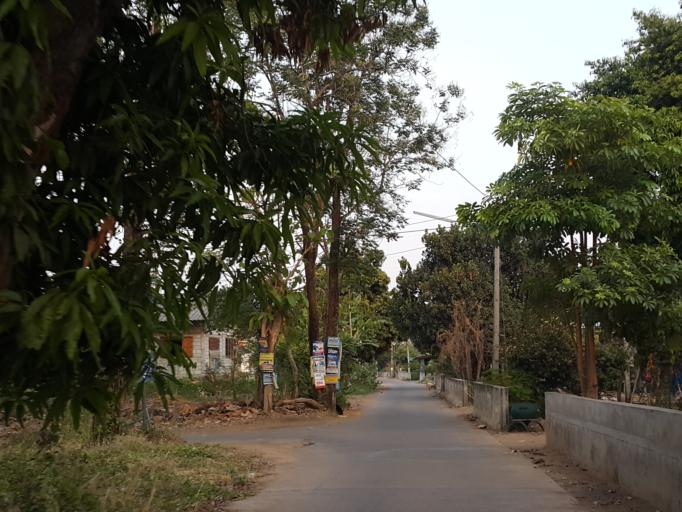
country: TH
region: Sukhothai
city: Sawankhalok
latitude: 17.2968
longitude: 99.8320
